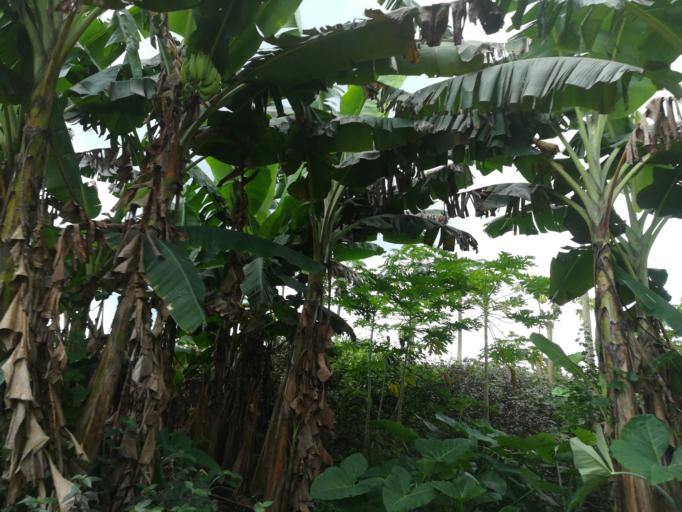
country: NG
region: Rivers
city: Okrika
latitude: 4.7263
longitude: 7.1448
